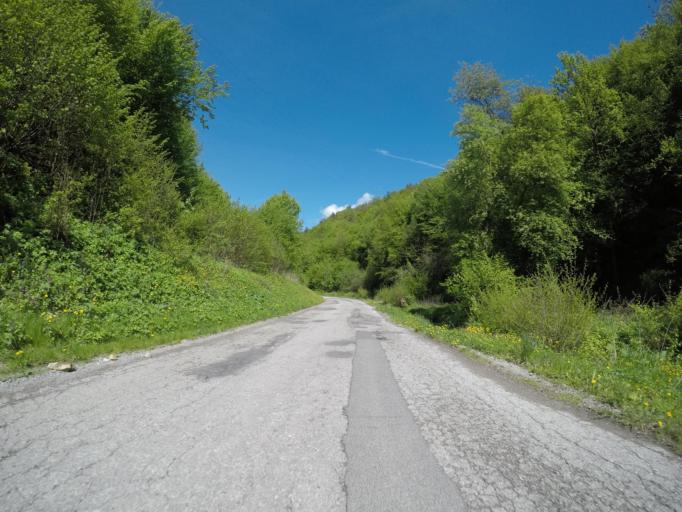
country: SK
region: Banskobystricky
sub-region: Okres Banska Bystrica
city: Banska Bystrica
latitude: 48.7232
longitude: 19.2184
